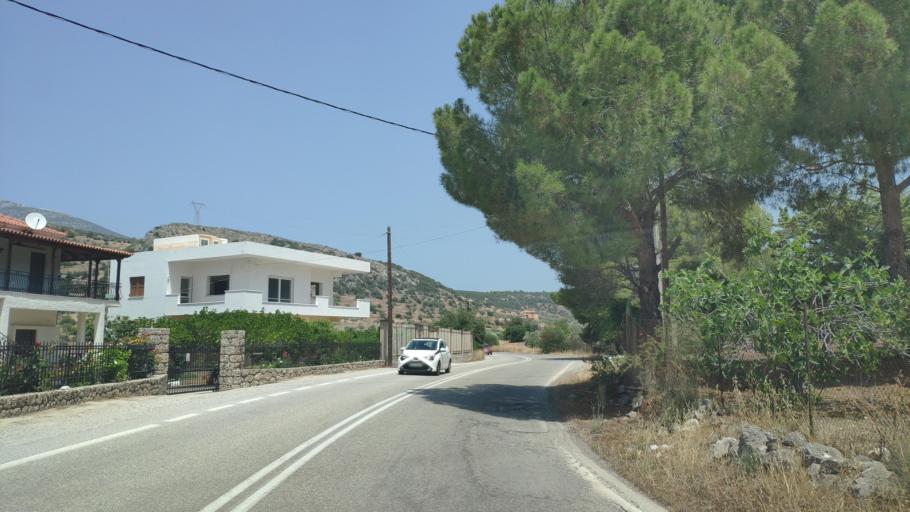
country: GR
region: Peloponnese
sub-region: Nomos Argolidos
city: Didyma
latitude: 37.4330
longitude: 23.1821
